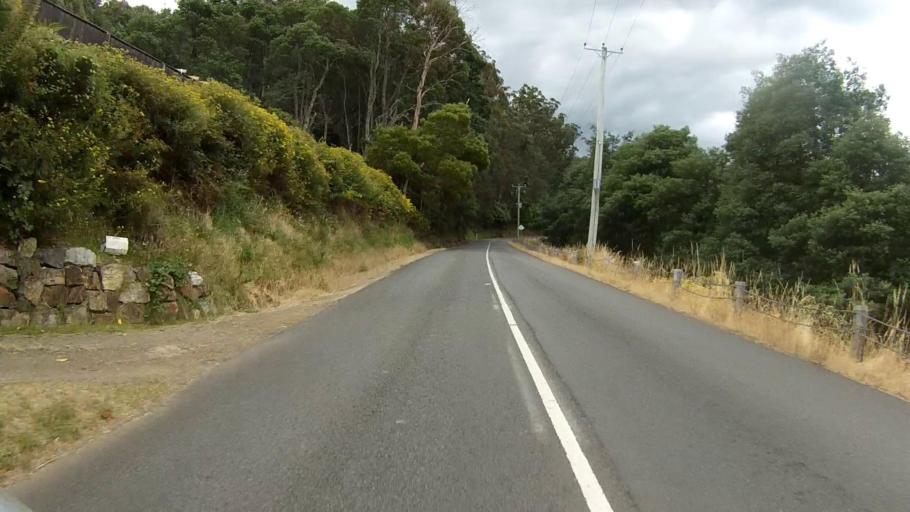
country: AU
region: Tasmania
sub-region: Kingborough
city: Kingston
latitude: -42.9537
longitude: 147.2269
